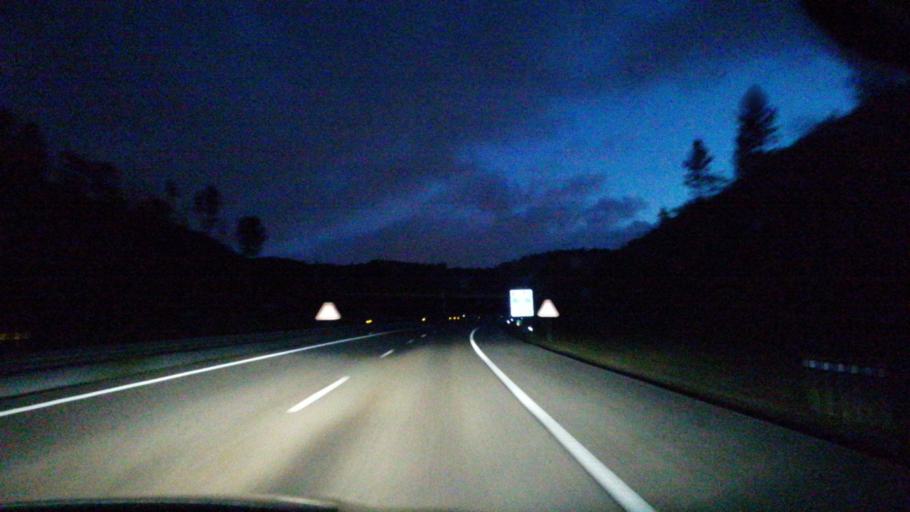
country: PT
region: Porto
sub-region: Lousada
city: Lousada
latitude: 41.3097
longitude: -8.2590
